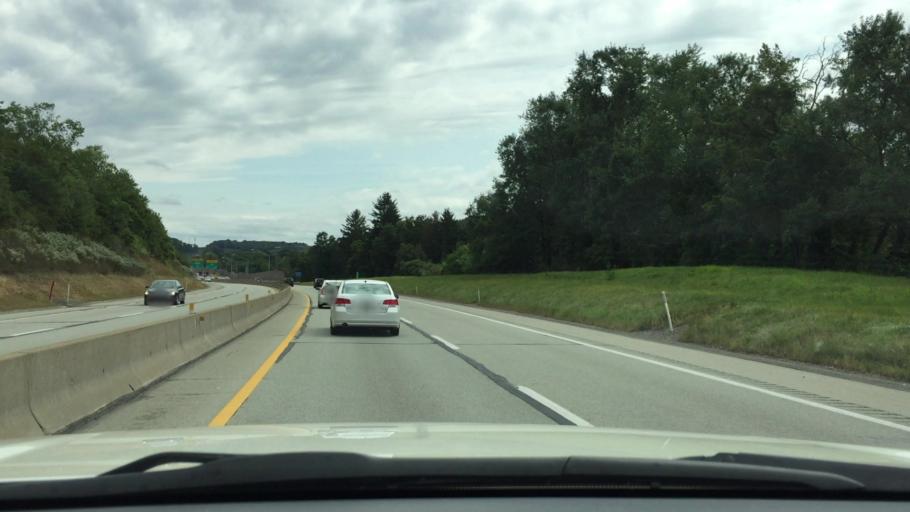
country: US
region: Pennsylvania
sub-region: Allegheny County
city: Bradford Woods
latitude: 40.6568
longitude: -80.0813
